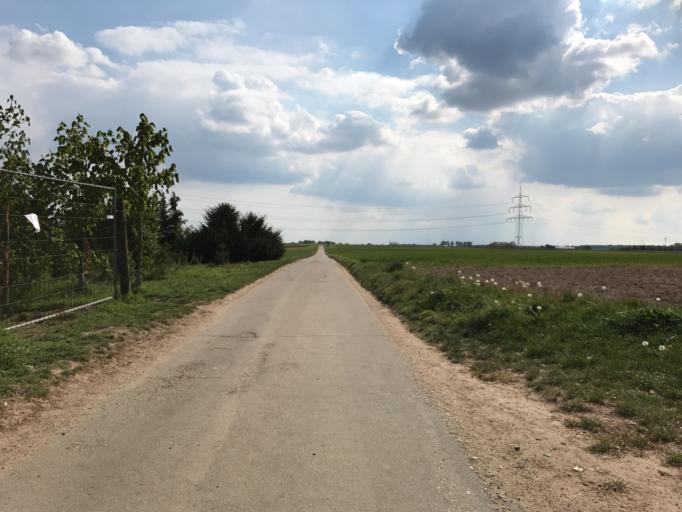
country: DE
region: Rheinland-Pfalz
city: Mainz
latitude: 49.9539
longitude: 8.2767
